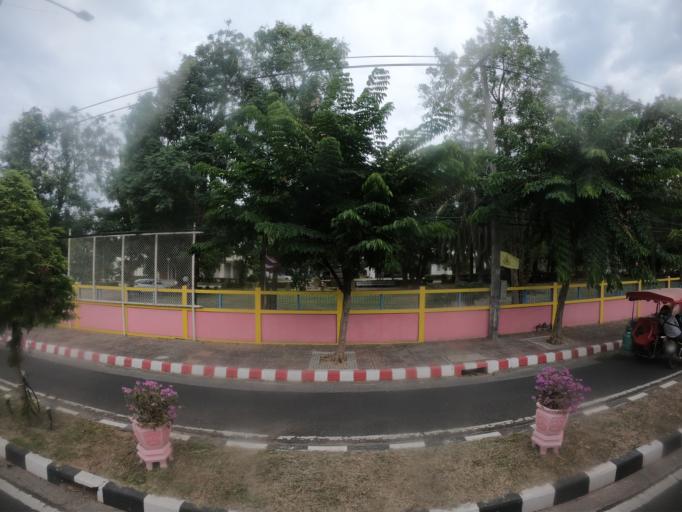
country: TH
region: Maha Sarakham
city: Maha Sarakham
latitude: 16.1865
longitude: 103.3009
